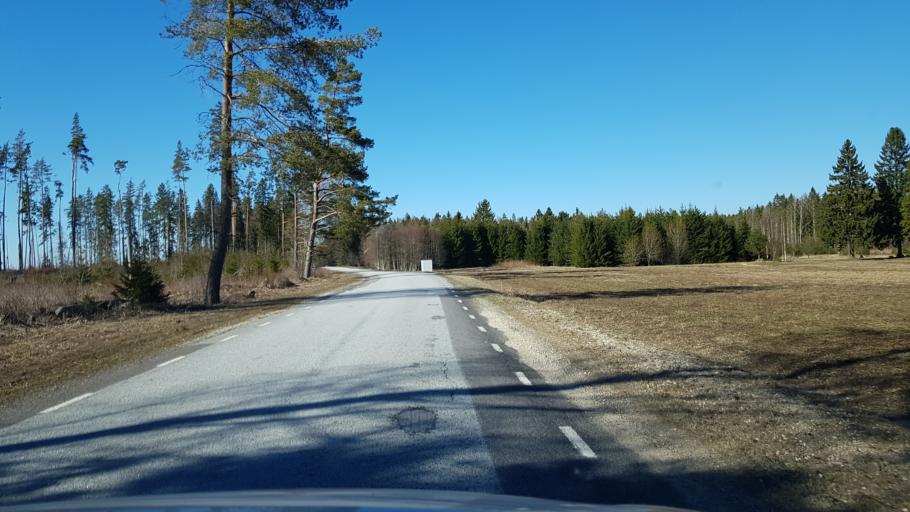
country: EE
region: Laeaene-Virumaa
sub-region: Viru-Nigula vald
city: Kunda
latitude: 59.3772
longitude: 26.5780
